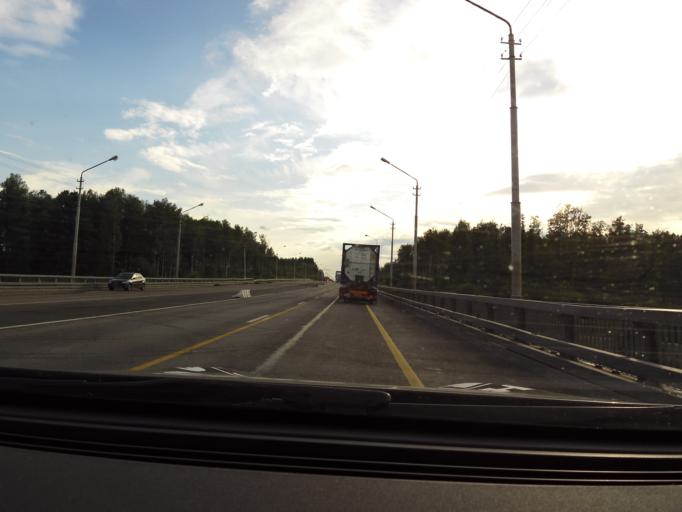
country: RU
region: Vladimir
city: Sudogda
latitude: 56.1053
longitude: 40.7889
